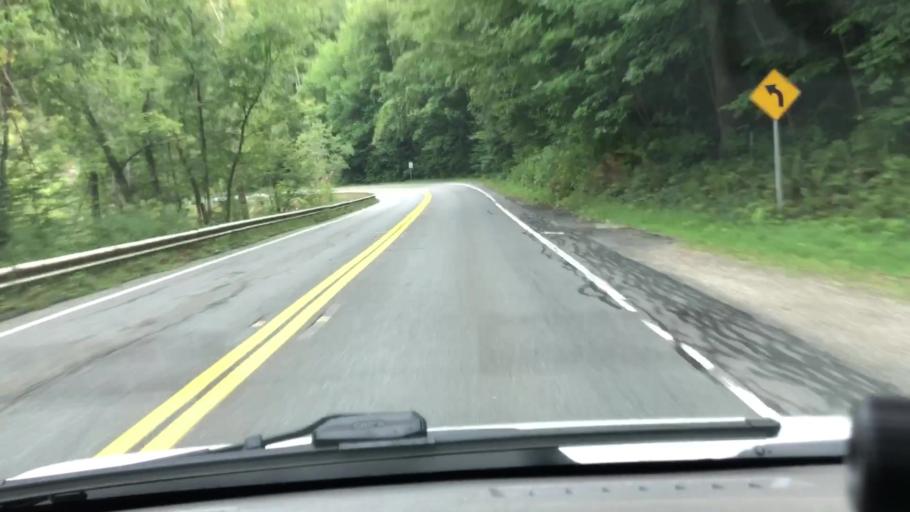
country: US
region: Massachusetts
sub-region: Franklin County
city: Charlemont
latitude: 42.6333
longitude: -72.9711
